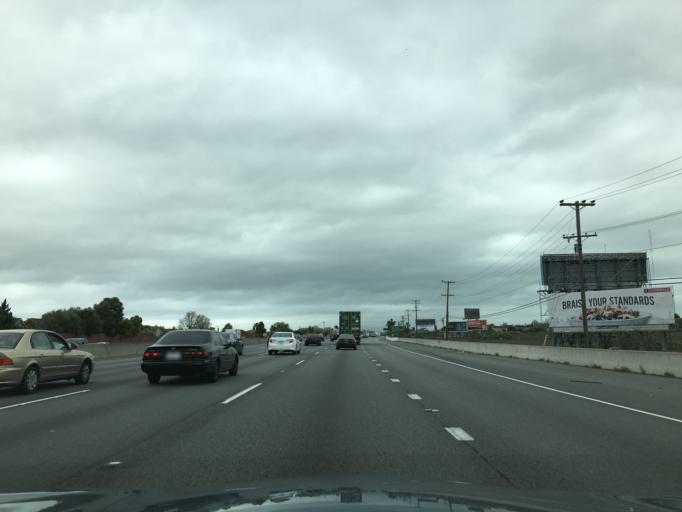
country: US
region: California
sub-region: San Mateo County
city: Belmont
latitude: 37.5301
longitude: -122.2742
